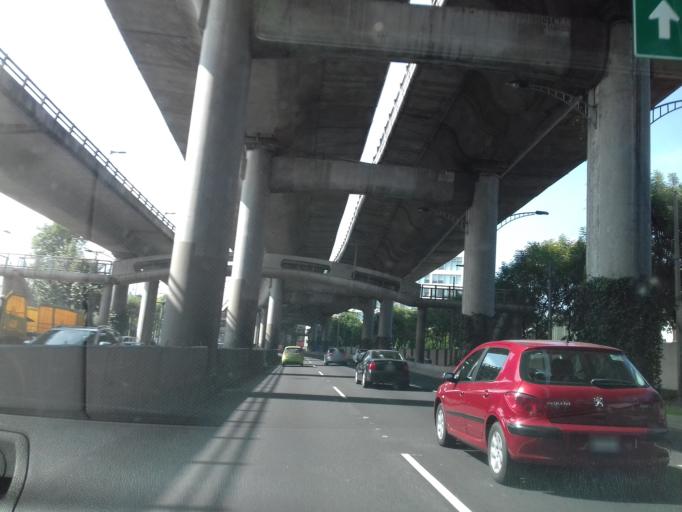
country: MX
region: Mexico City
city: Alvaro Obregon
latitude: 19.3543
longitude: -99.2002
